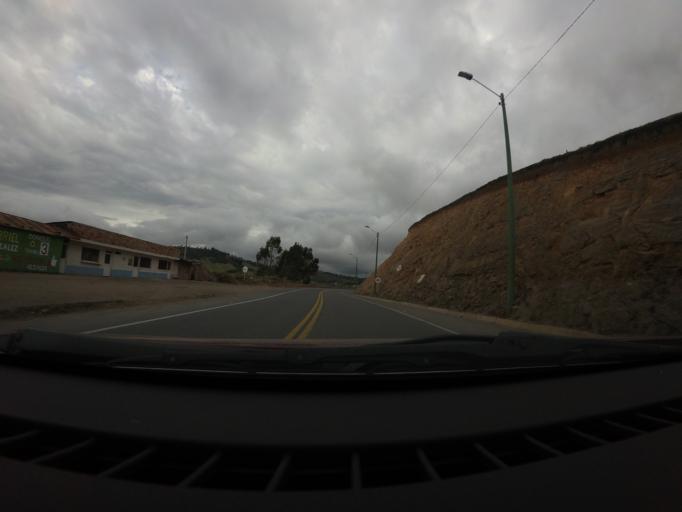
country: CO
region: Boyaca
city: Tunja
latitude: 5.5052
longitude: -73.3755
